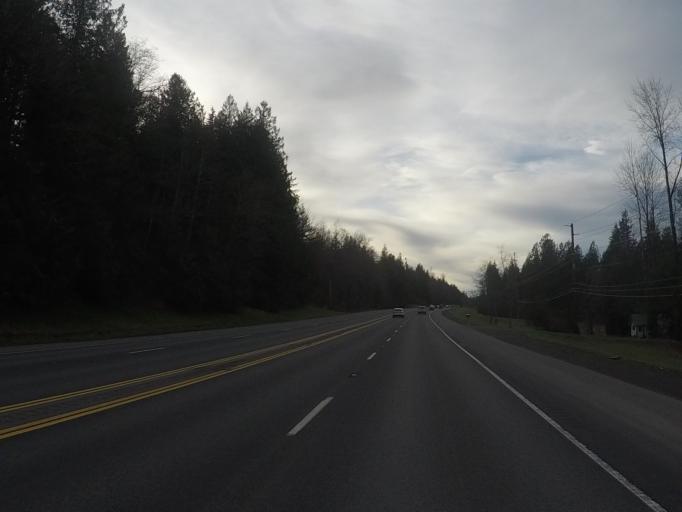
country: US
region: Oregon
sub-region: Clackamas County
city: Mount Hood Village
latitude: 45.3762
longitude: -122.0887
